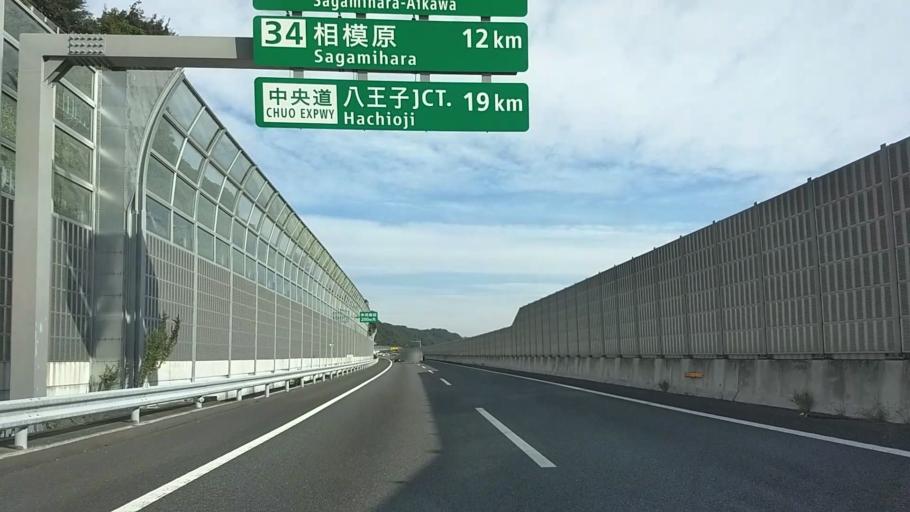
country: JP
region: Kanagawa
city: Zama
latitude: 35.4947
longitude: 139.3676
